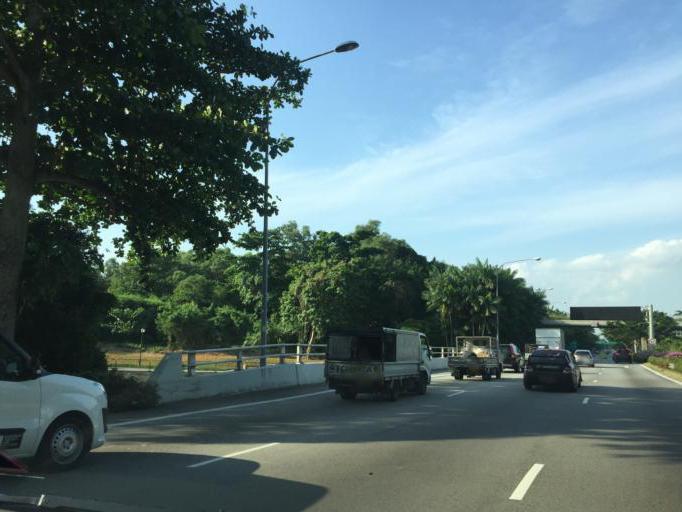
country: SG
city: Singapore
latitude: 1.3356
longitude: 103.9398
